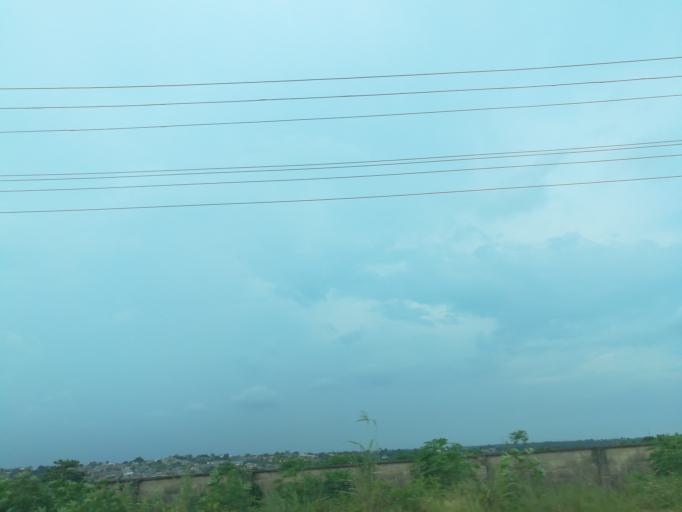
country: NG
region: Lagos
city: Ikorodu
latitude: 6.6545
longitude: 3.6695
